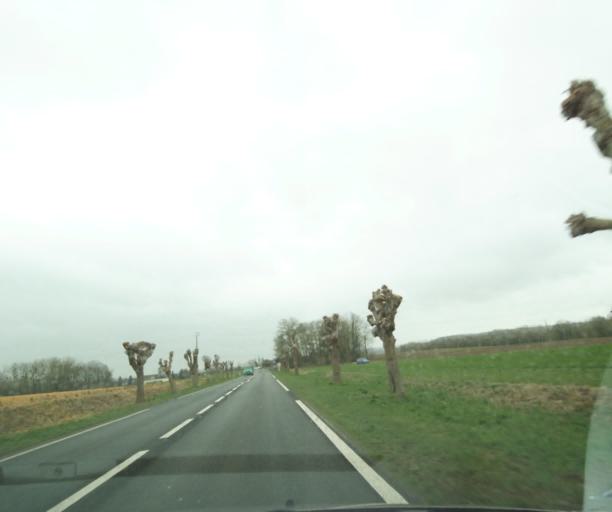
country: FR
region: Picardie
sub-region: Departement de l'Oise
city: Noyon
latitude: 49.5952
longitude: 3.0059
